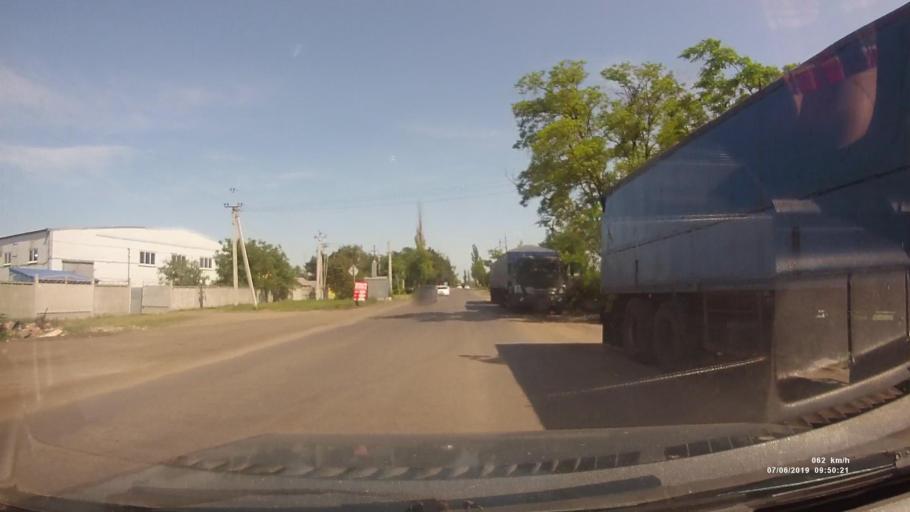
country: RU
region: Rostov
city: Azov
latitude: 47.0789
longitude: 39.4375
